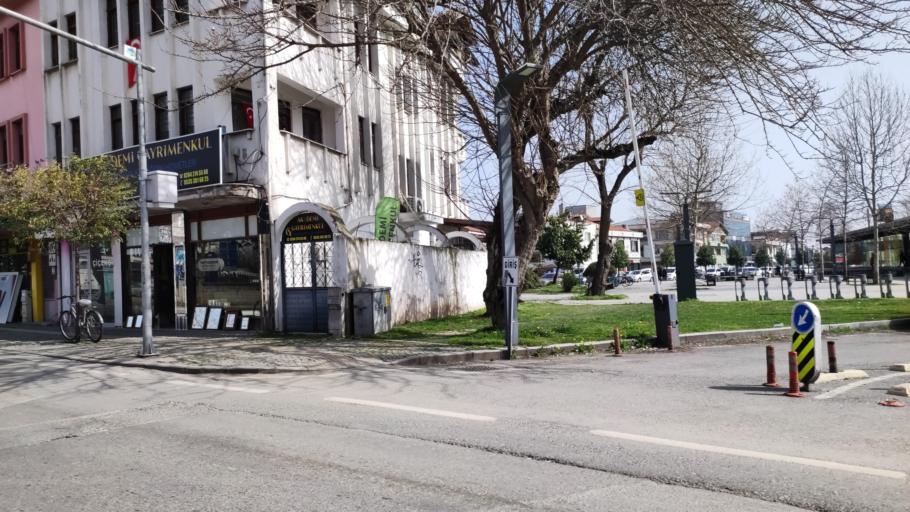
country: TR
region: Sakarya
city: Adapazari
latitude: 40.7726
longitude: 30.3918
